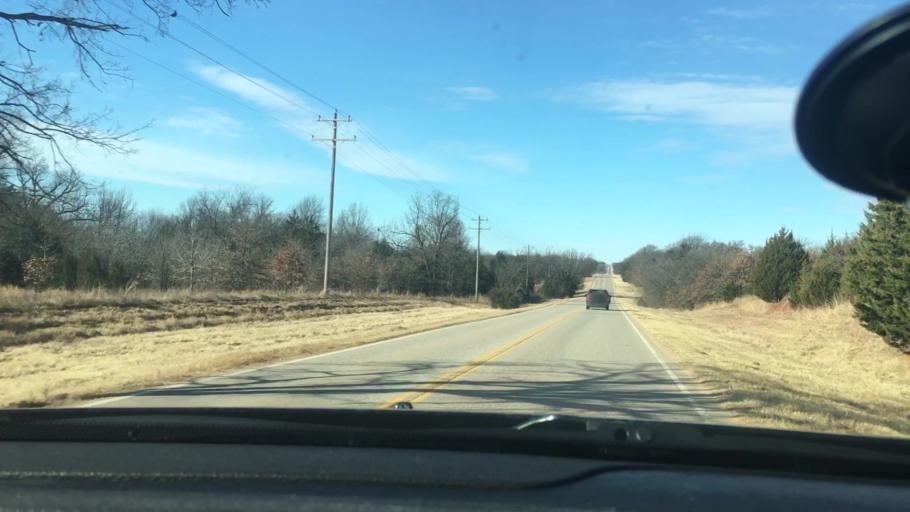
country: US
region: Oklahoma
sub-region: Cleveland County
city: Lexington
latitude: 35.0148
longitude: -97.1316
